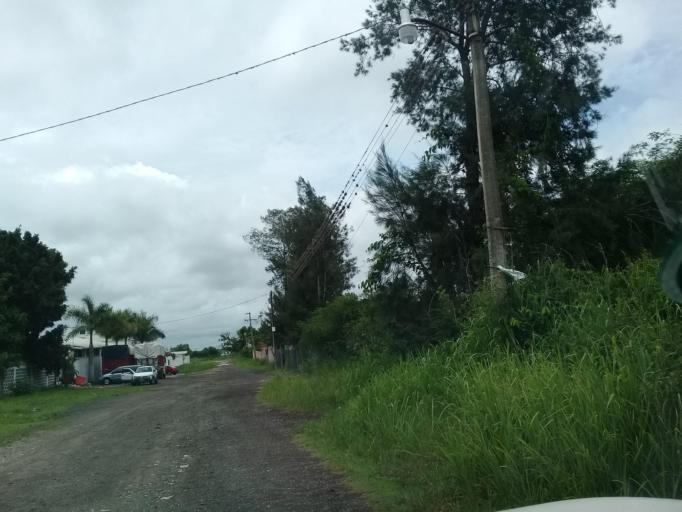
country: MX
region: Veracruz
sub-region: Emiliano Zapata
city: Dos Rios
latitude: 19.4816
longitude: -96.7923
